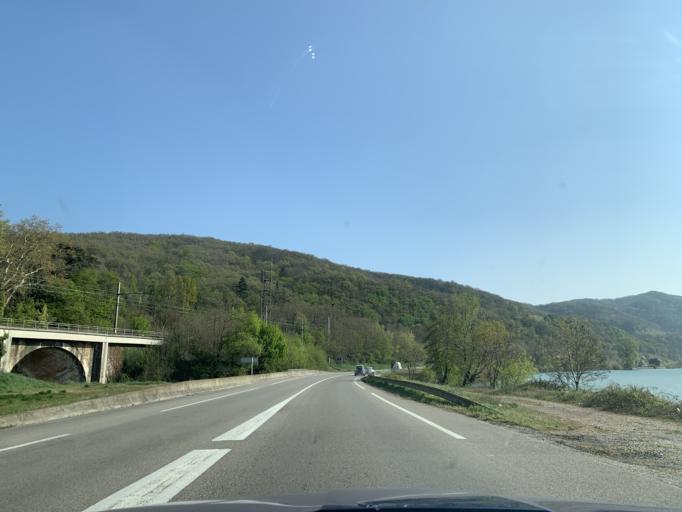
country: FR
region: Rhone-Alpes
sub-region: Departement de la Drome
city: Saint-Vallier
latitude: 45.1577
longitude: 4.8323
